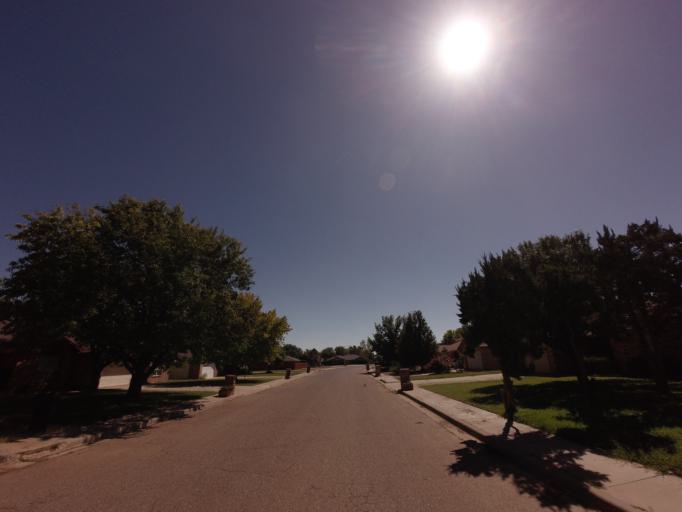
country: US
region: New Mexico
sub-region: Curry County
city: Clovis
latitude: 34.4468
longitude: -103.1813
